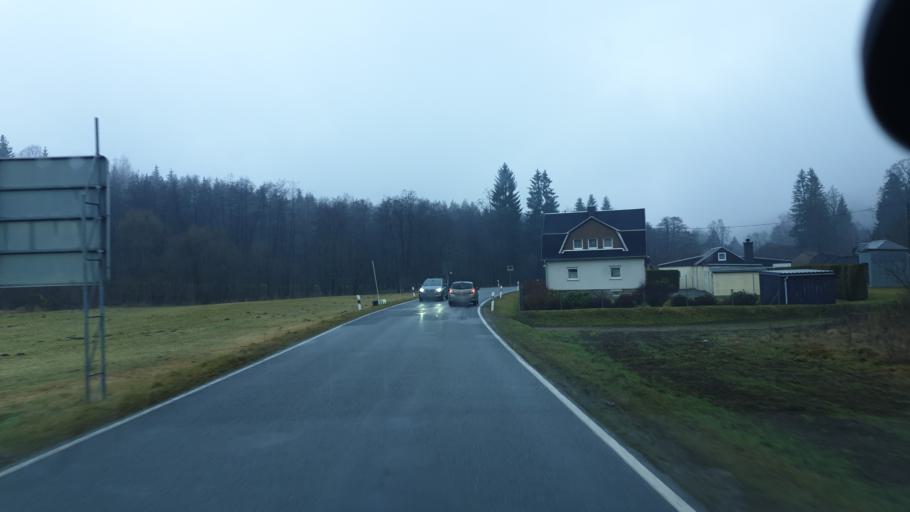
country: DE
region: Saxony
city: Seiffen
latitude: 50.6280
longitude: 13.4090
